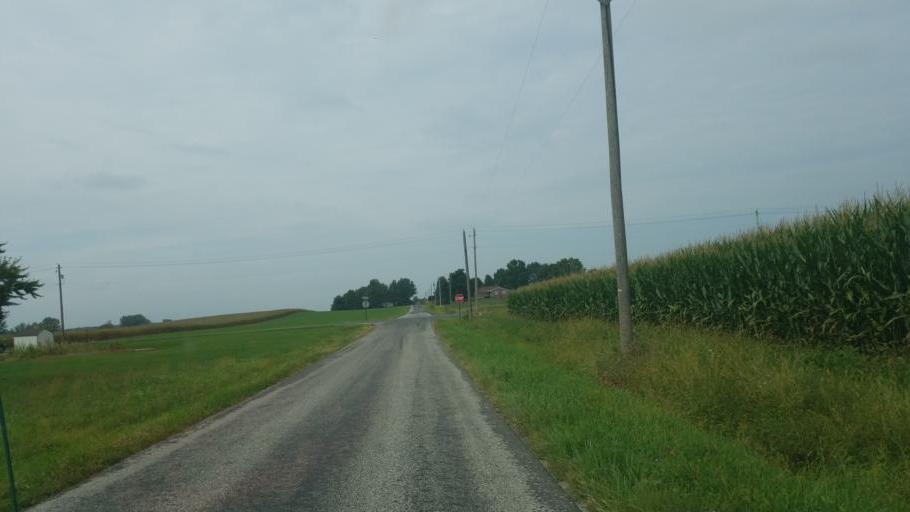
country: US
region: Ohio
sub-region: Wayne County
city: Rittman
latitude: 40.9652
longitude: -81.8124
